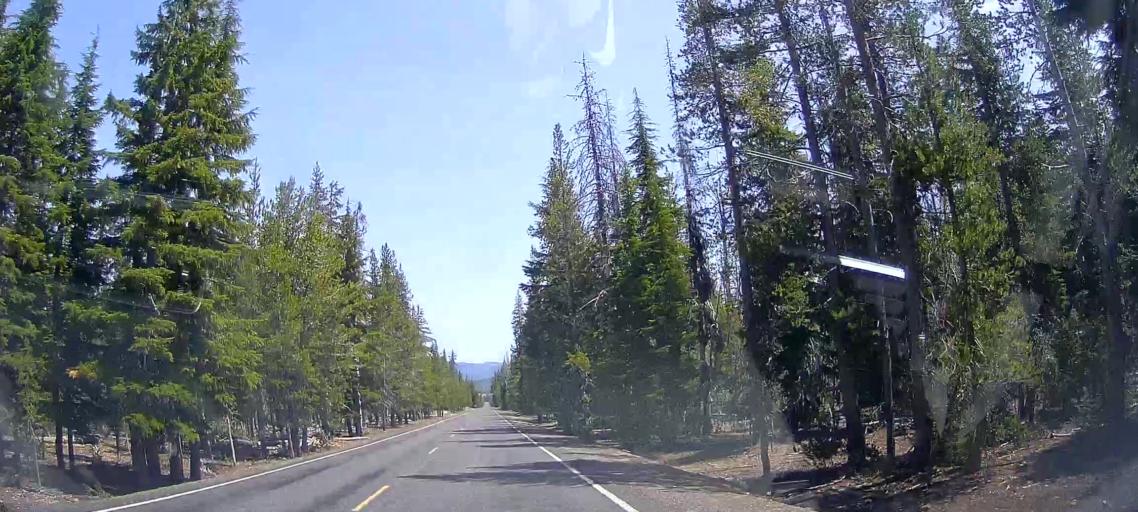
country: US
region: Oregon
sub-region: Jackson County
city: Shady Cove
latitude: 43.0104
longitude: -122.1304
